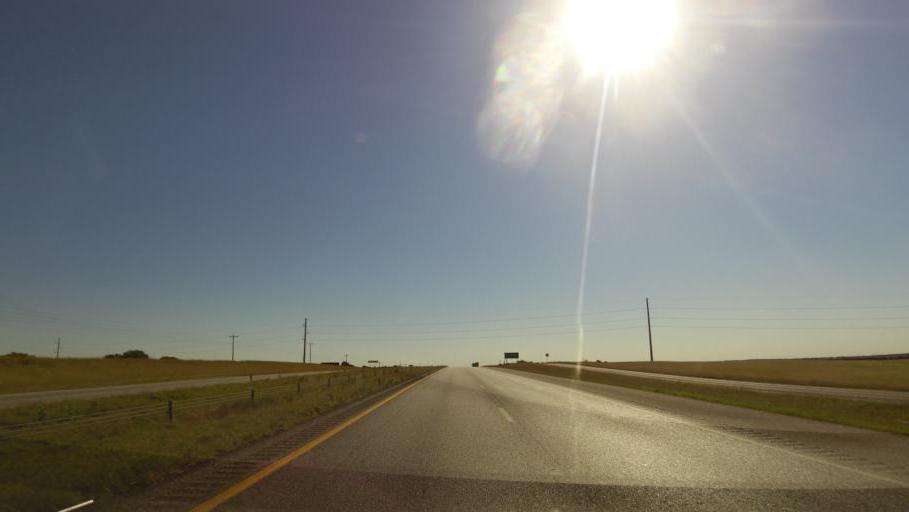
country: US
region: Texas
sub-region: Guadalupe County
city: McQueeney
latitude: 29.5447
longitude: -98.0591
